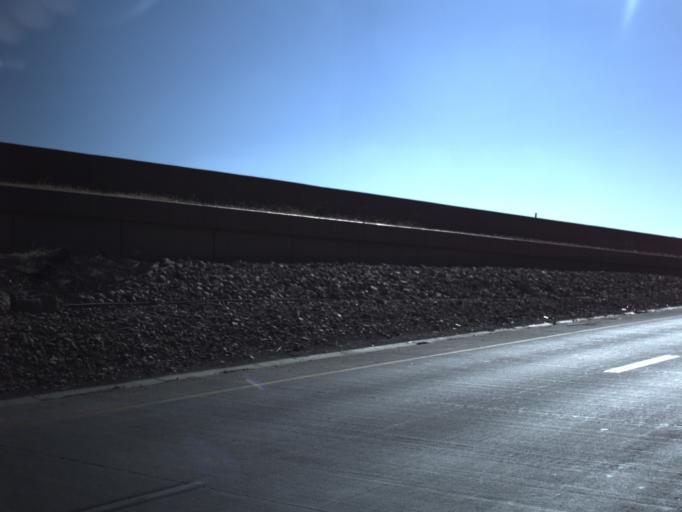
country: US
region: Utah
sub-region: Salt Lake County
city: South Salt Lake
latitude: 40.7244
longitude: -111.9403
